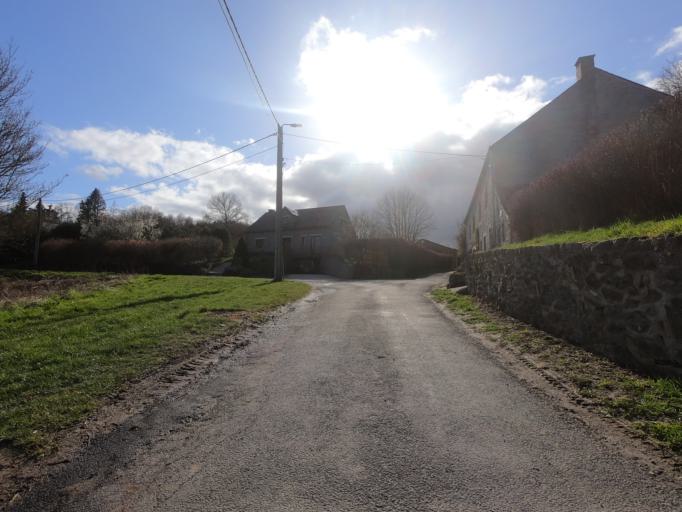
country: BE
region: Wallonia
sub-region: Province de Namur
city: Mettet
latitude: 50.2944
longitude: 4.7528
